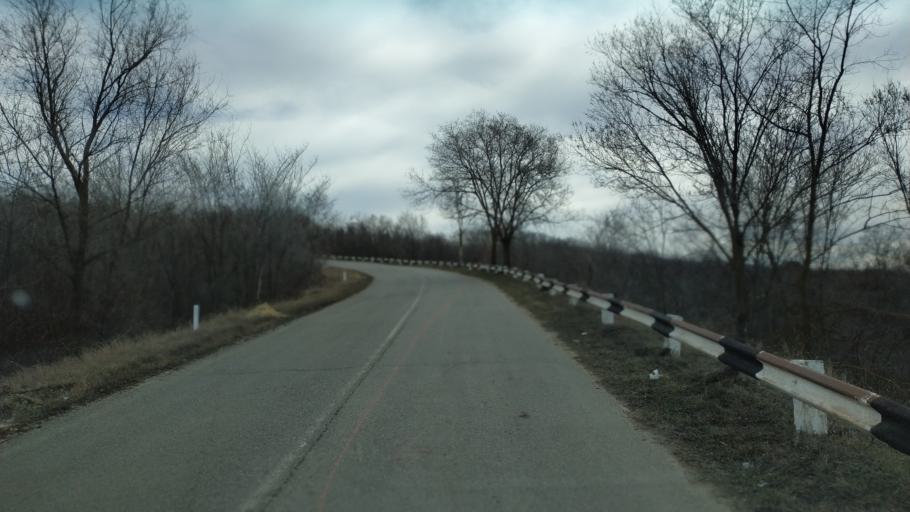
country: MD
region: Nisporeni
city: Nisporeni
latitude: 46.9553
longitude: 28.2302
